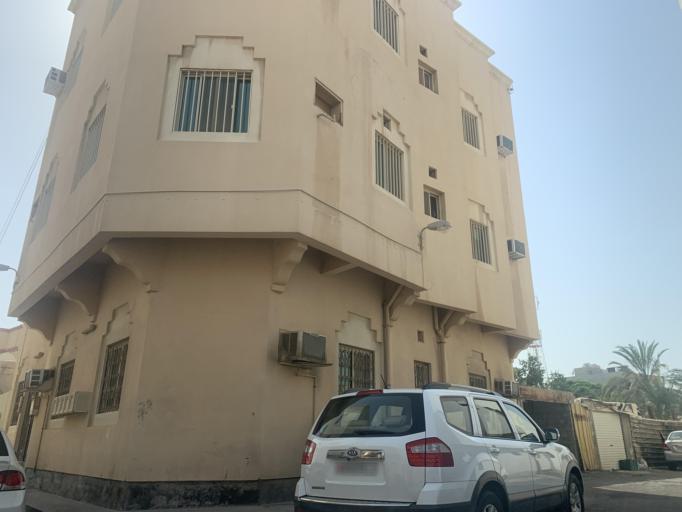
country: BH
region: Northern
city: Madinat `Isa
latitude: 26.1948
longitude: 50.4881
